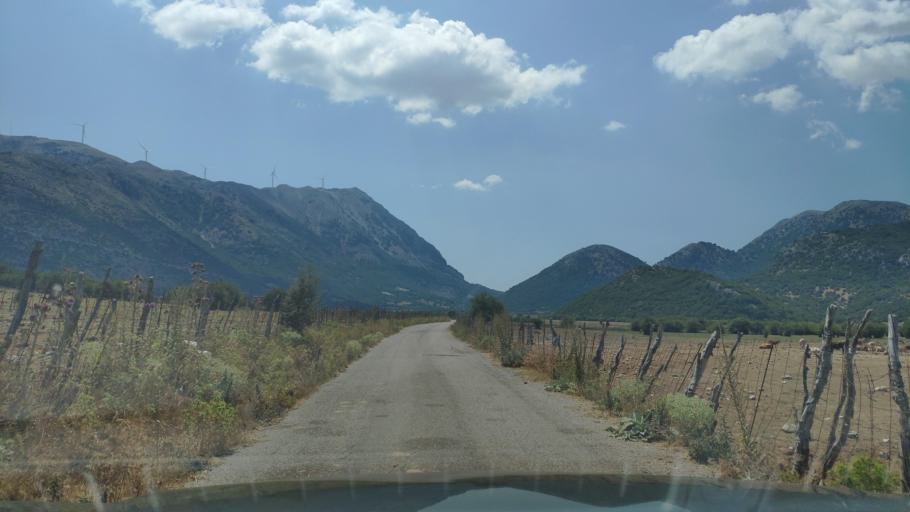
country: GR
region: West Greece
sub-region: Nomos Aitolias kai Akarnanias
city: Monastirakion
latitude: 38.7923
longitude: 20.9606
